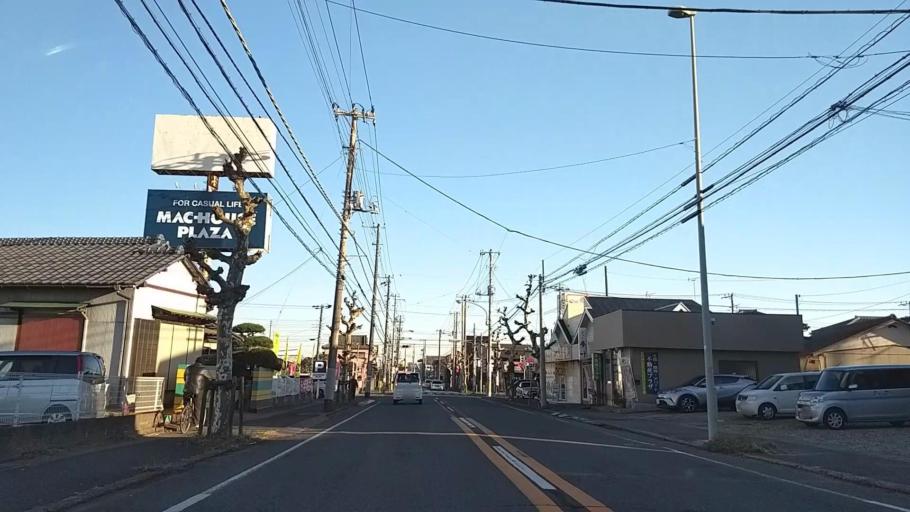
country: JP
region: Chiba
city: Hasaki
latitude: 35.7354
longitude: 140.8084
